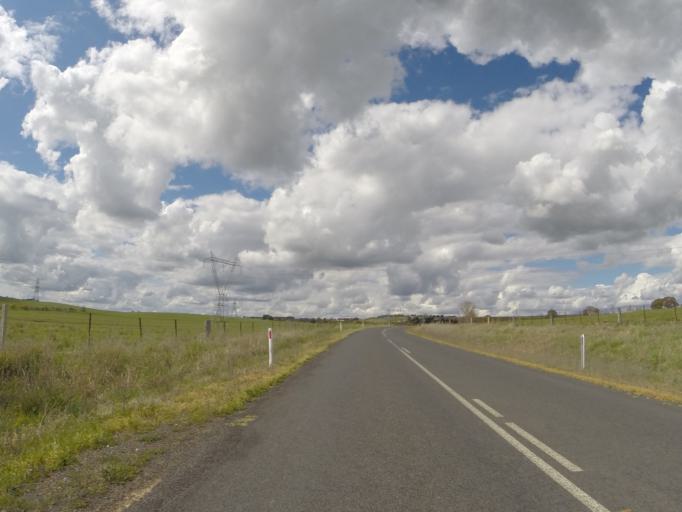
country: AU
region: New South Wales
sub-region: Yass Valley
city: Yass
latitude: -34.8748
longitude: 148.9058
